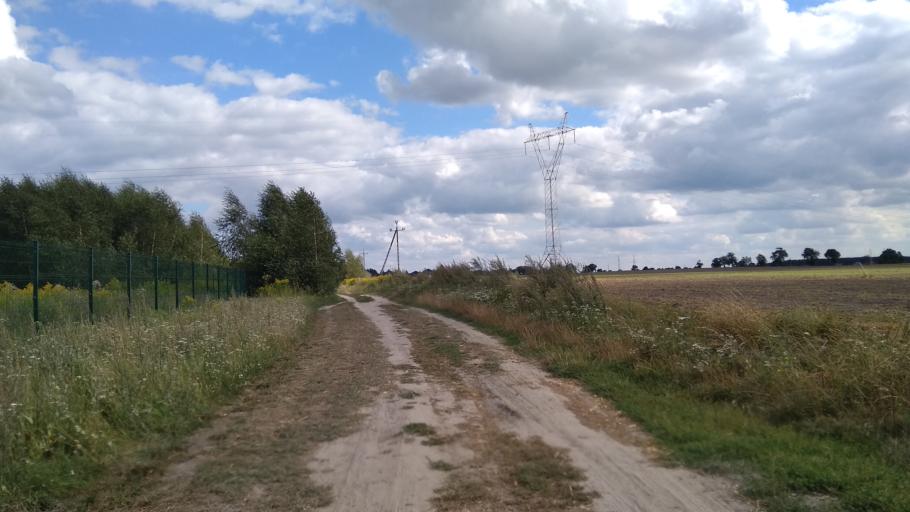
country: PL
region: Kujawsko-Pomorskie
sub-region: Powiat bydgoski
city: Osielsko
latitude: 53.2222
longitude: 18.1407
